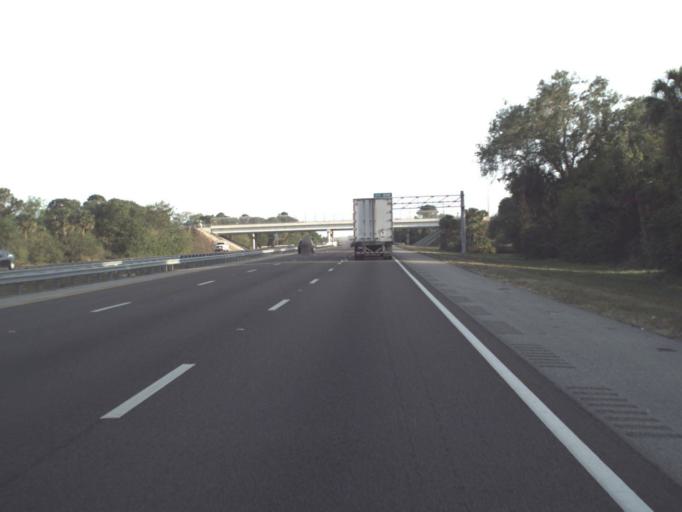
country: US
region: Florida
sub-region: Brevard County
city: Port Saint John
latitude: 28.4679
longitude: -80.8214
